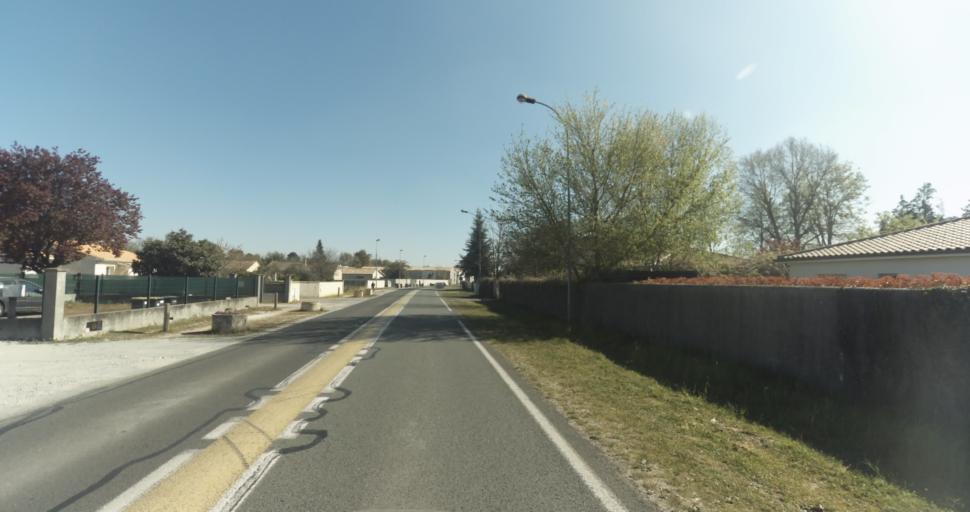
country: FR
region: Aquitaine
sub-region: Departement de la Gironde
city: Martignas-sur-Jalle
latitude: 44.7975
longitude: -0.8391
